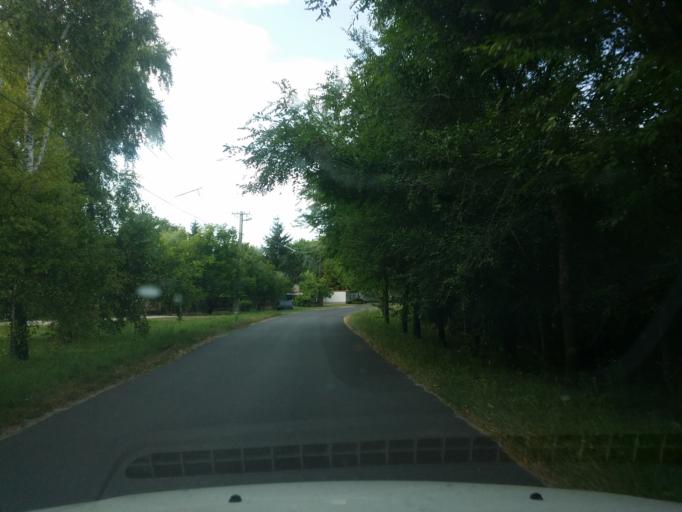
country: HU
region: Bacs-Kiskun
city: Jaszszentlaszlo
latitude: 46.5689
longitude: 19.7652
